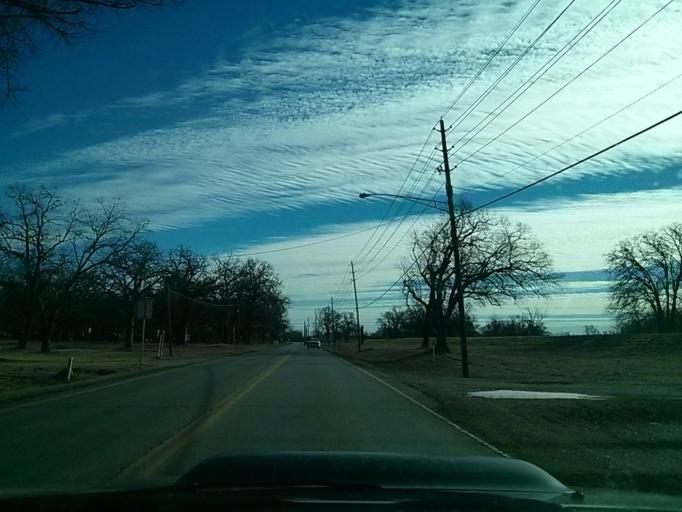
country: US
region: Oklahoma
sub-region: Tulsa County
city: Jenks
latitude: 36.0242
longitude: -95.9897
